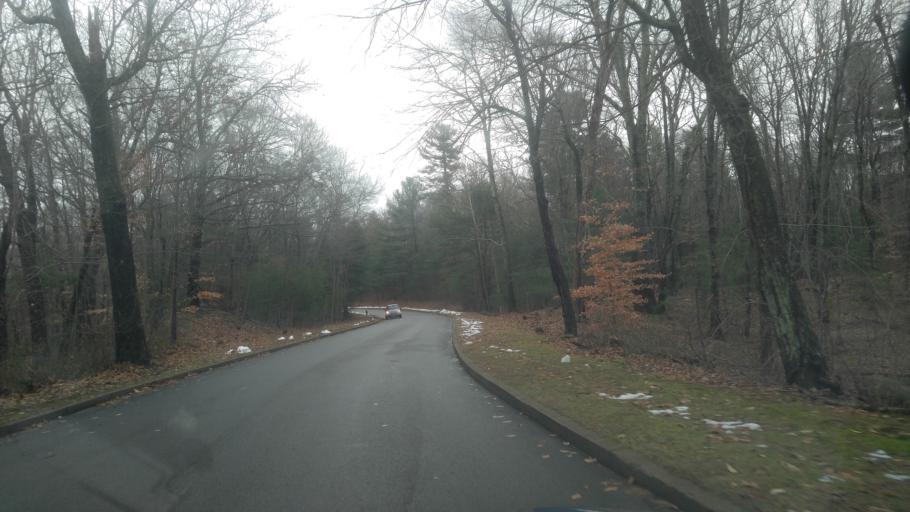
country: US
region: Rhode Island
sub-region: Kent County
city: West Warwick
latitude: 41.6525
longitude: -71.5370
